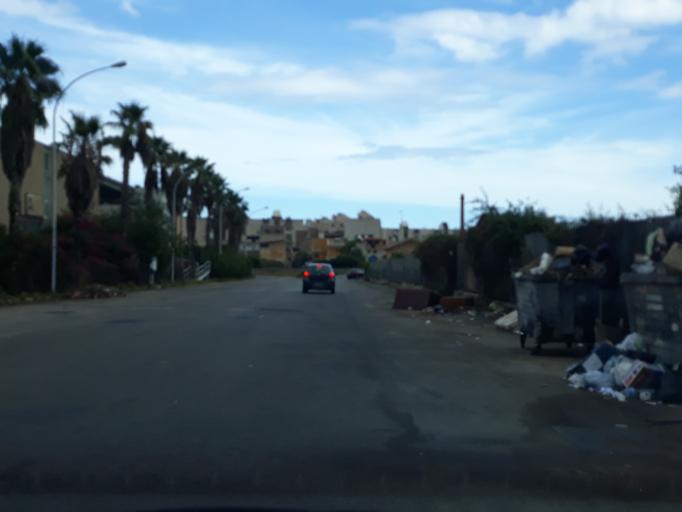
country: IT
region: Sicily
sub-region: Palermo
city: Ciaculli
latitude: 38.0911
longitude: 13.4070
